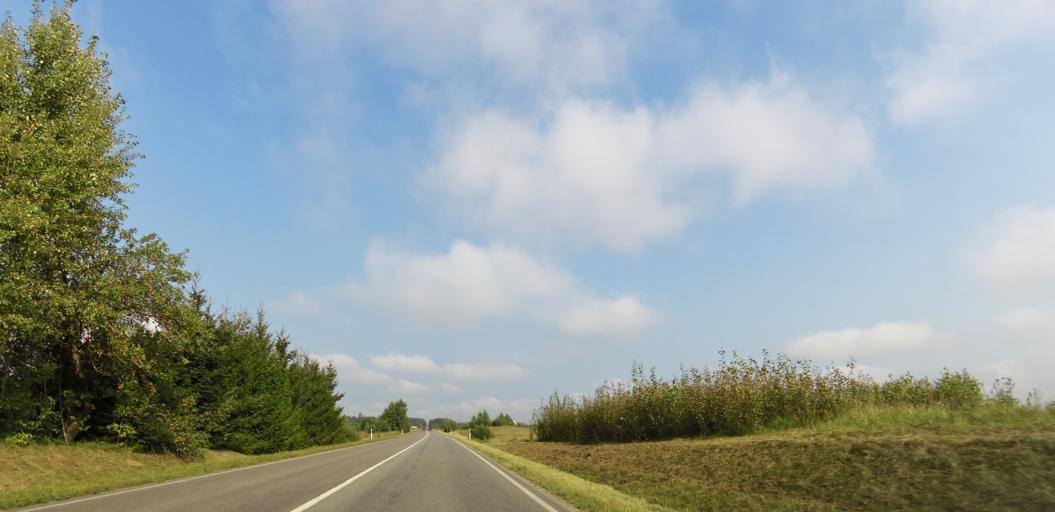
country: LT
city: Grigiskes
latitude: 54.7578
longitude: 25.0814
